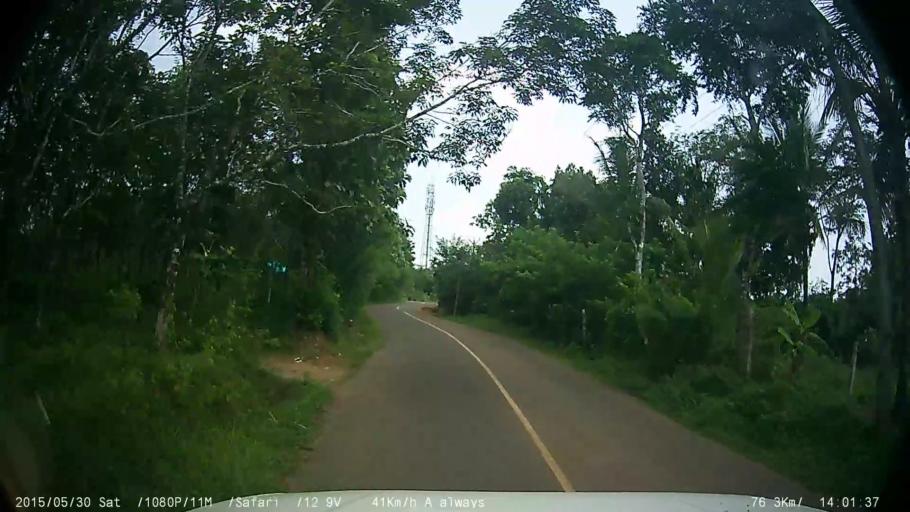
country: IN
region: Kerala
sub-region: Wayanad
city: Panamaram
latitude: 11.8222
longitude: 76.0627
